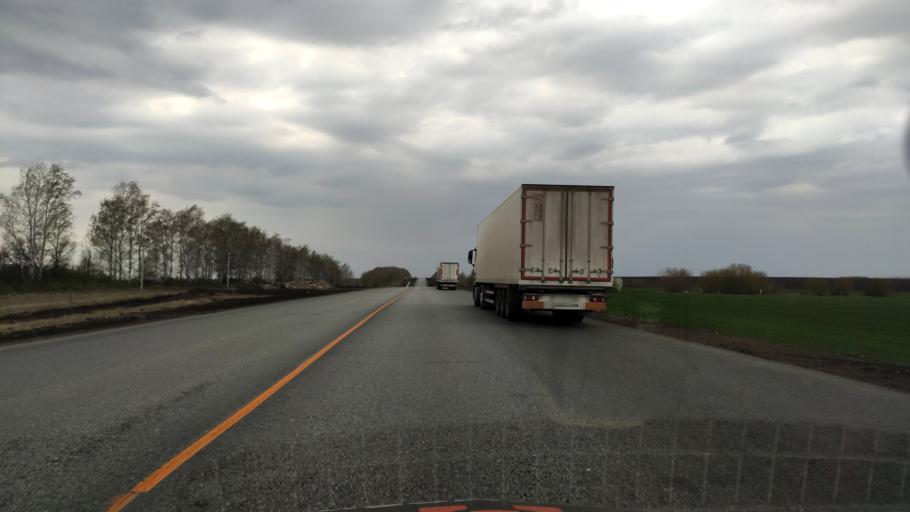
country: RU
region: Kursk
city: Gorshechnoye
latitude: 51.5485
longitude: 38.1135
